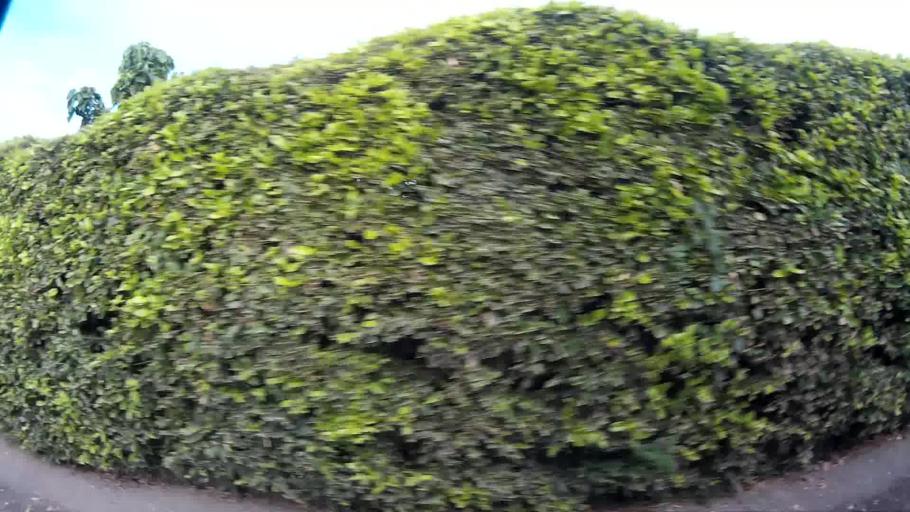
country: CO
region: Valle del Cauca
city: Ulloa
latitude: 4.7378
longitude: -75.7388
